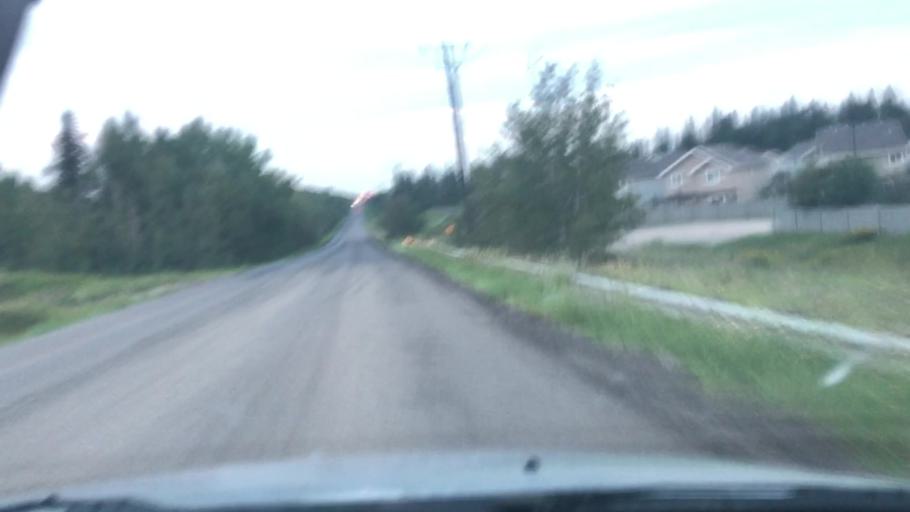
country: CA
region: Alberta
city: Devon
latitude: 53.4864
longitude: -113.6889
